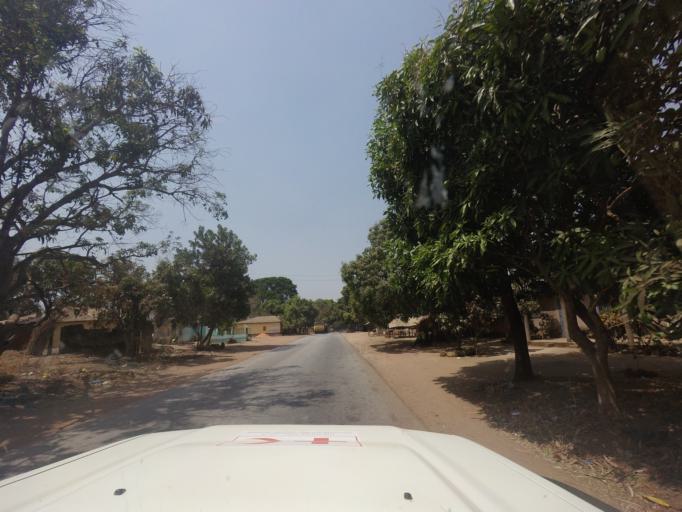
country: GN
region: Kindia
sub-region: Kindia
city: Kindia
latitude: 9.9324
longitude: -12.9868
